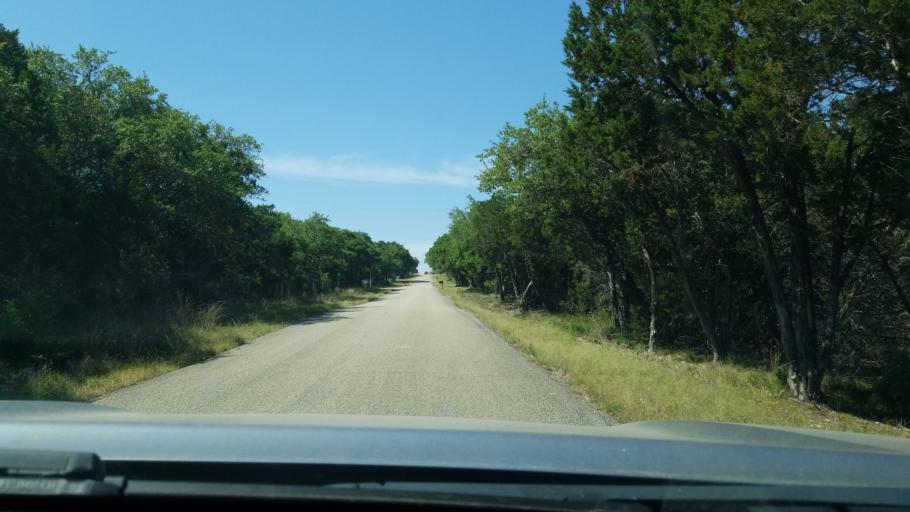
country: US
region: Texas
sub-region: Comal County
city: Bulverde
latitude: 29.7606
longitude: -98.5153
